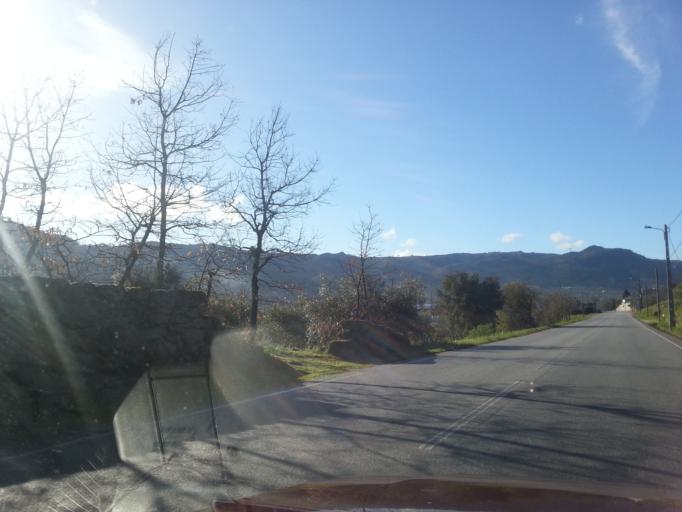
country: PT
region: Guarda
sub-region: Guarda
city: Guarda
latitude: 40.6107
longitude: -7.3030
